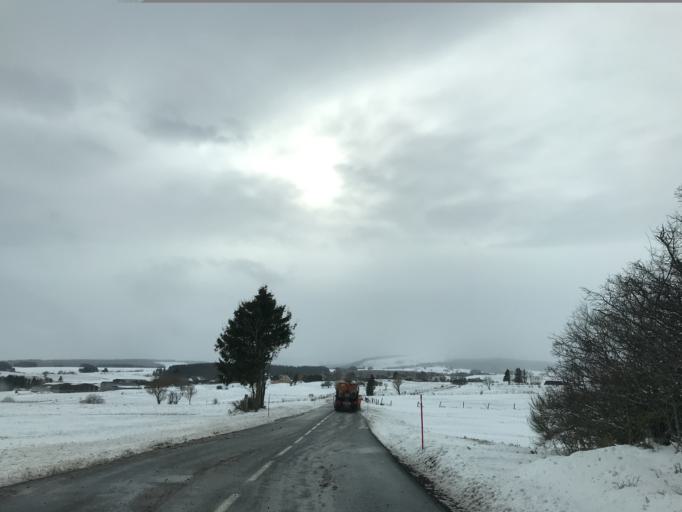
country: FR
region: Auvergne
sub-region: Departement du Puy-de-Dome
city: Aydat
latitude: 45.6588
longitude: 2.9210
